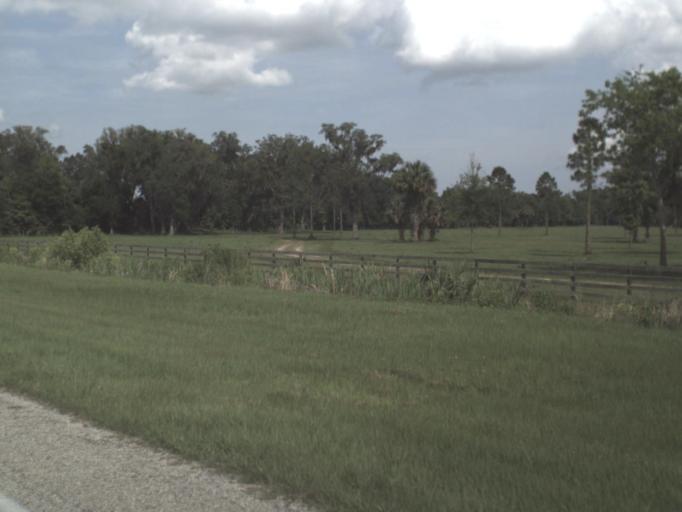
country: US
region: Florida
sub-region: Putnam County
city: East Palatka
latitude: 29.7067
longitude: -81.5374
